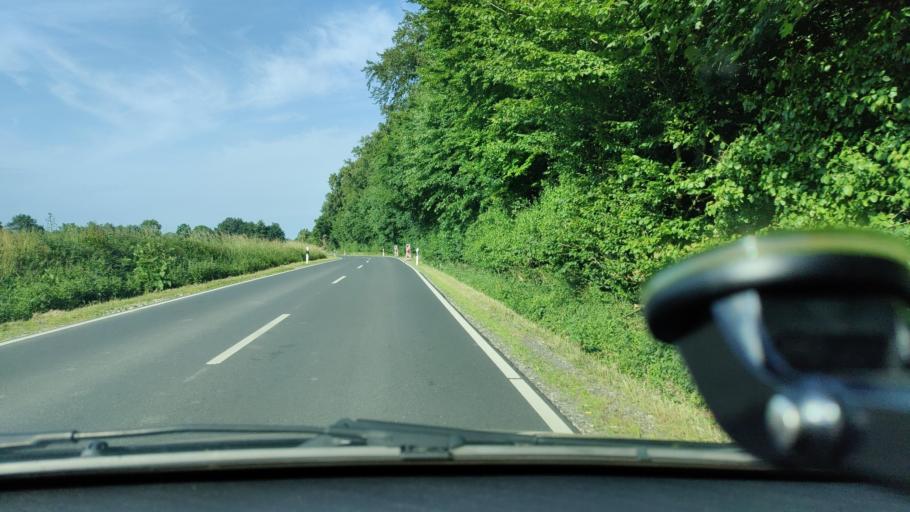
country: DE
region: North Rhine-Westphalia
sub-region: Regierungsbezirk Munster
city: Laer
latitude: 52.0471
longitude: 7.3388
